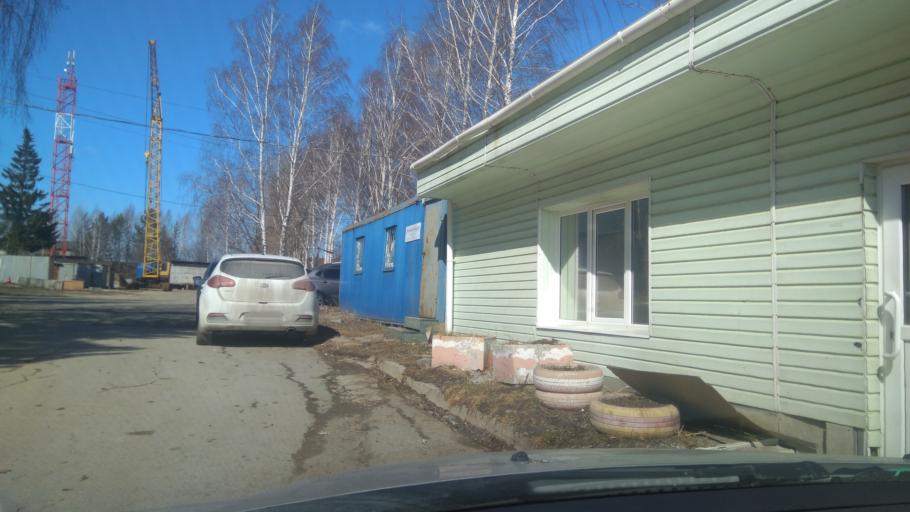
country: RU
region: Sverdlovsk
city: Verkhnyaya Pyshma
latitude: 56.9299
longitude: 60.6105
